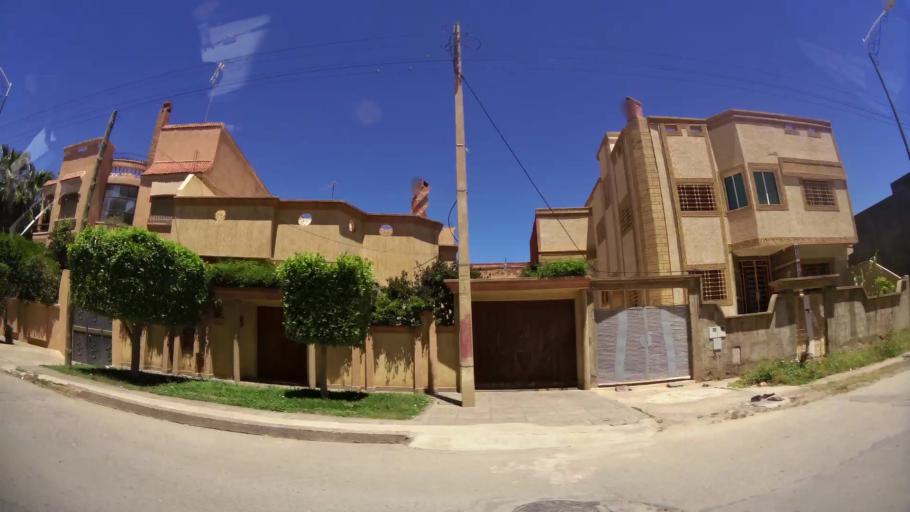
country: MA
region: Oriental
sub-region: Oujda-Angad
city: Oujda
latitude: 34.6761
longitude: -1.8750
